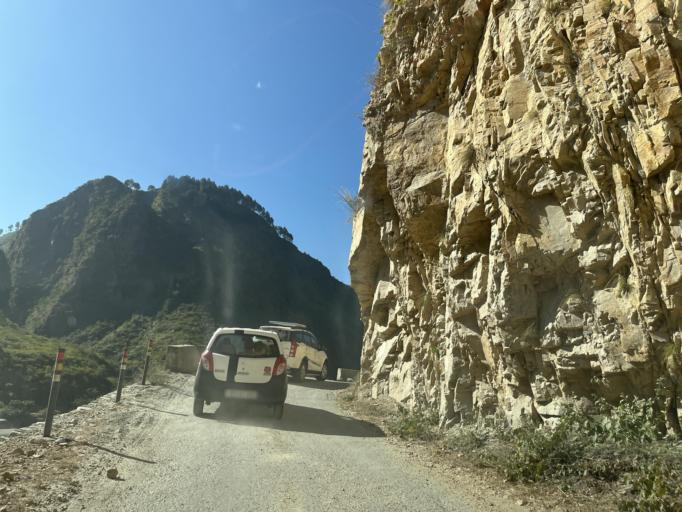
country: IN
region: Uttarakhand
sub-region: Naini Tal
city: Naini Tal
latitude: 29.5076
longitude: 79.4578
